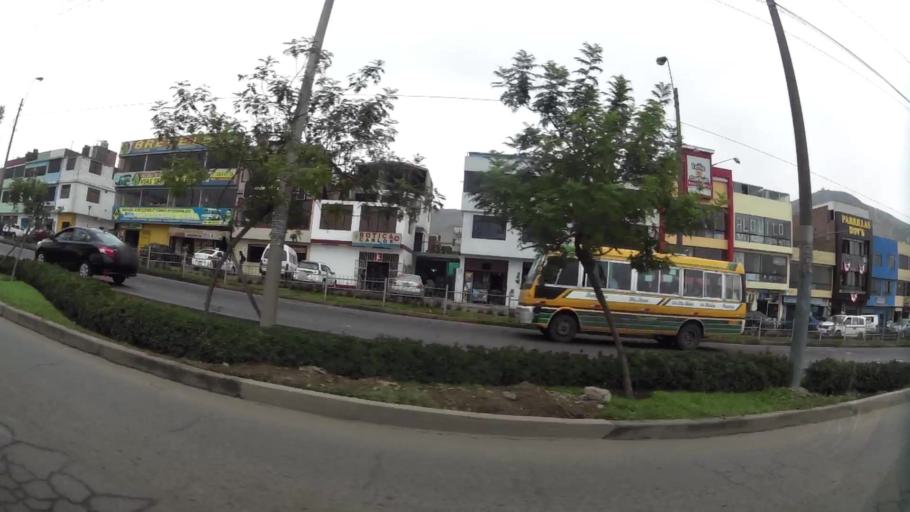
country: PE
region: Lima
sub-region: Lima
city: La Molina
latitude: -12.0855
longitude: -76.8886
